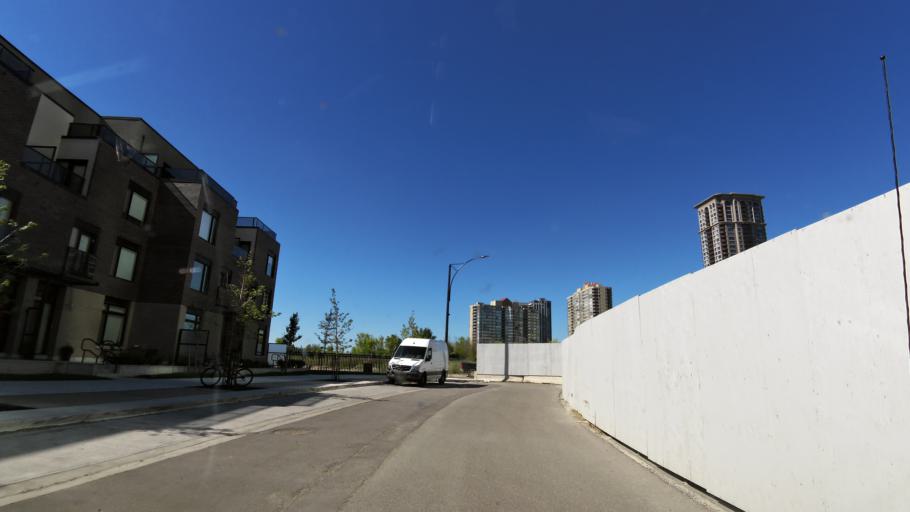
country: CA
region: Ontario
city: Mississauga
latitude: 43.5858
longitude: -79.6486
